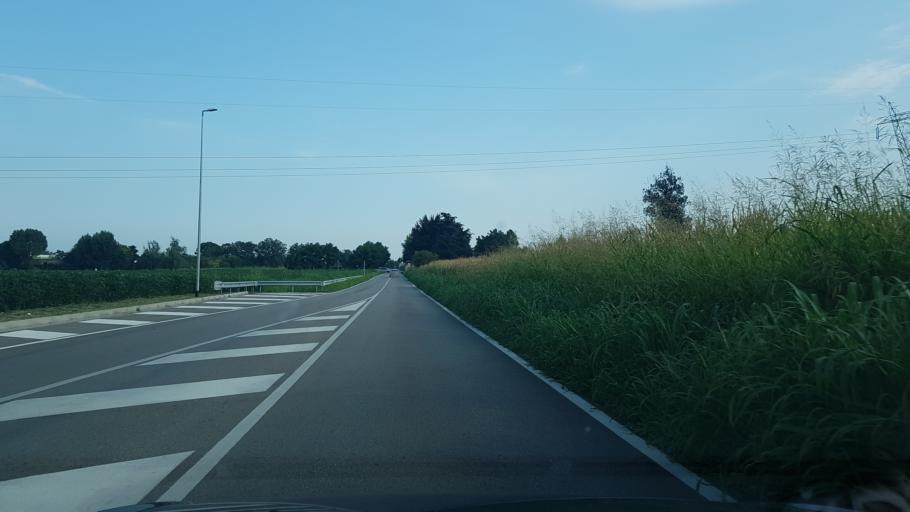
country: IT
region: Veneto
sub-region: Provincia di Vicenza
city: Giavenale
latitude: 45.6969
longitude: 11.4123
